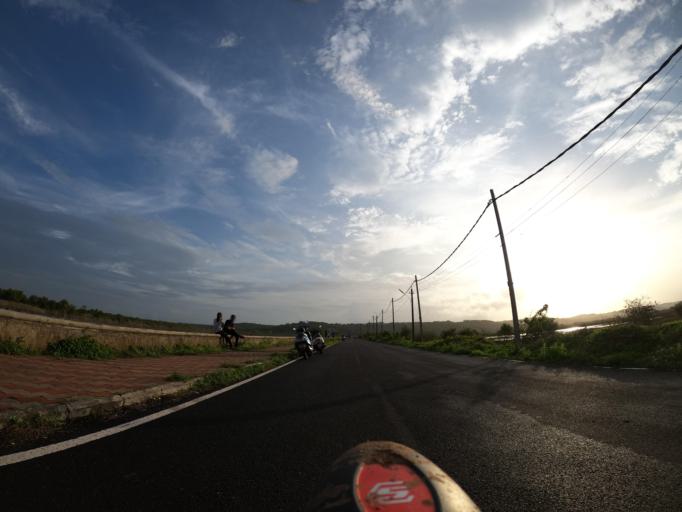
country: IN
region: Goa
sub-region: North Goa
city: Serula
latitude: 15.5284
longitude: 73.8572
